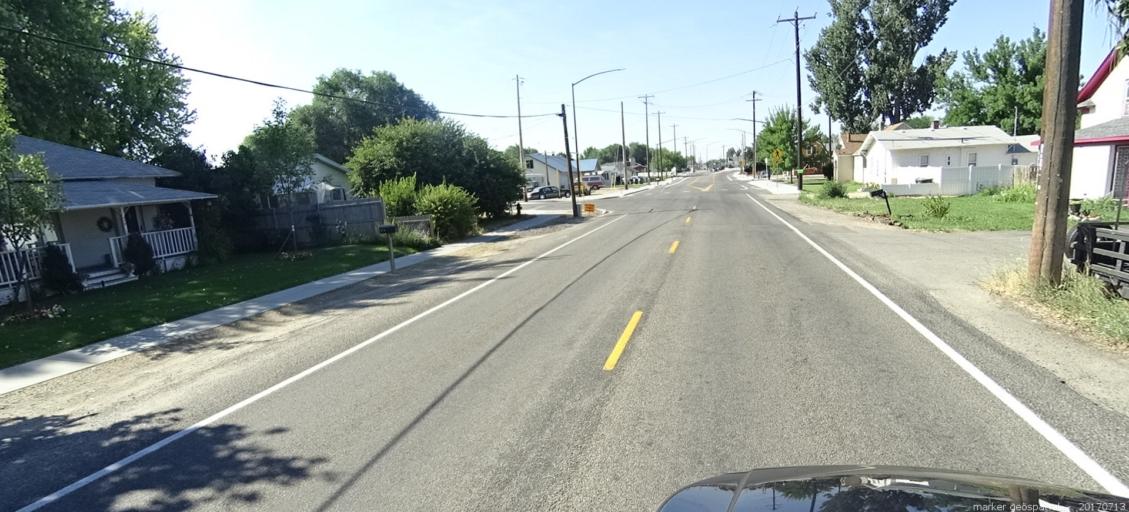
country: US
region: Idaho
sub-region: Ada County
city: Kuna
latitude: 43.4926
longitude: -116.4137
